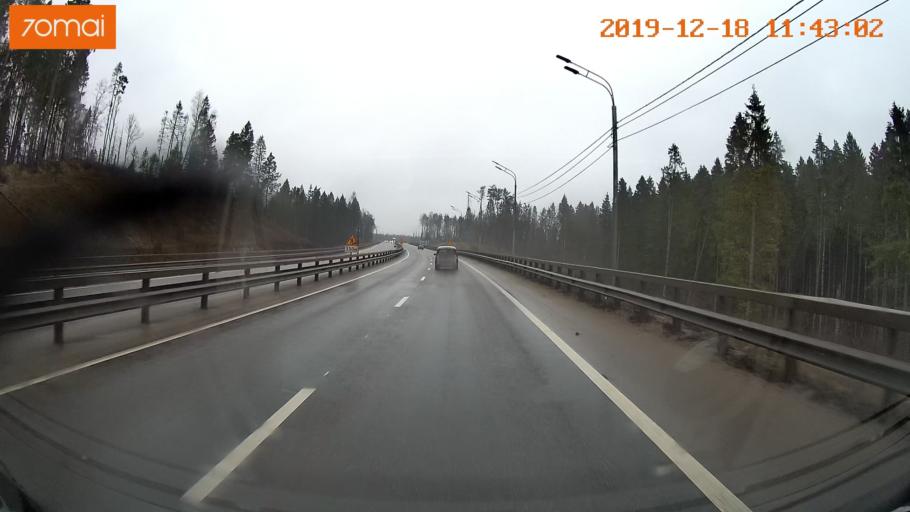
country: RU
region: Moskovskaya
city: Zvenigorod
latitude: 55.7301
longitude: 36.8798
